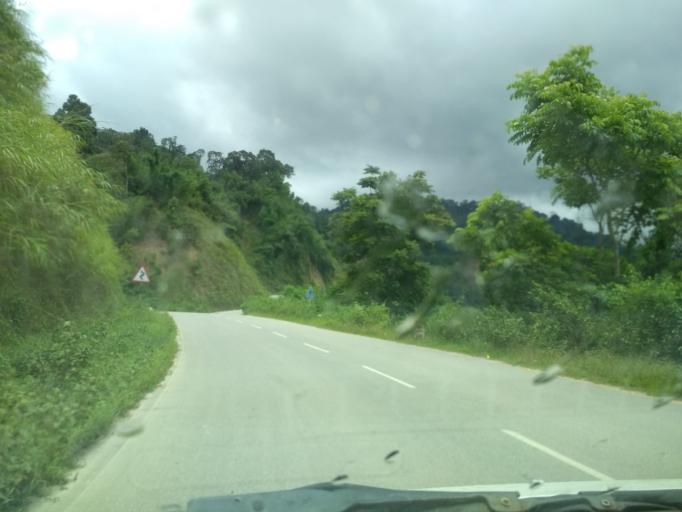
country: IN
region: Arunachal Pradesh
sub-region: Papum Pare
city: Naharlagun
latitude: 27.1868
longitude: 93.7840
